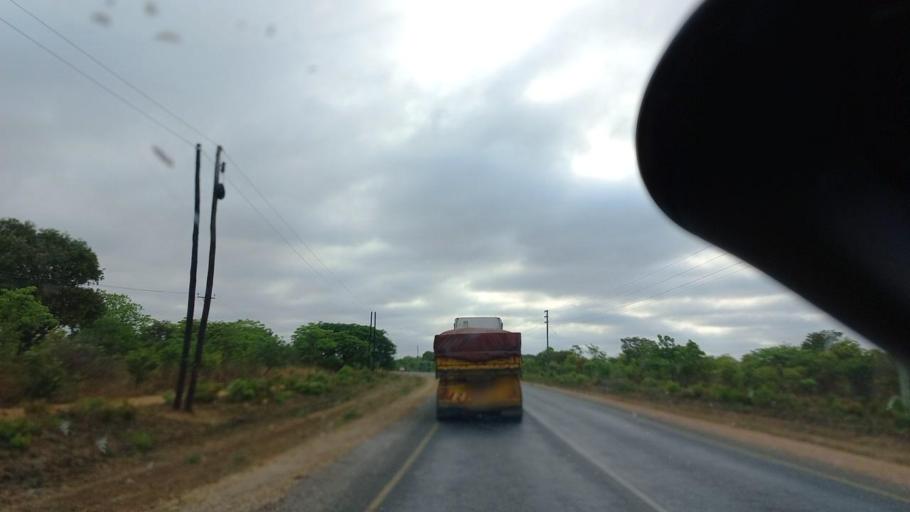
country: ZM
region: Lusaka
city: Chongwe
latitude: -15.3530
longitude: 28.5455
